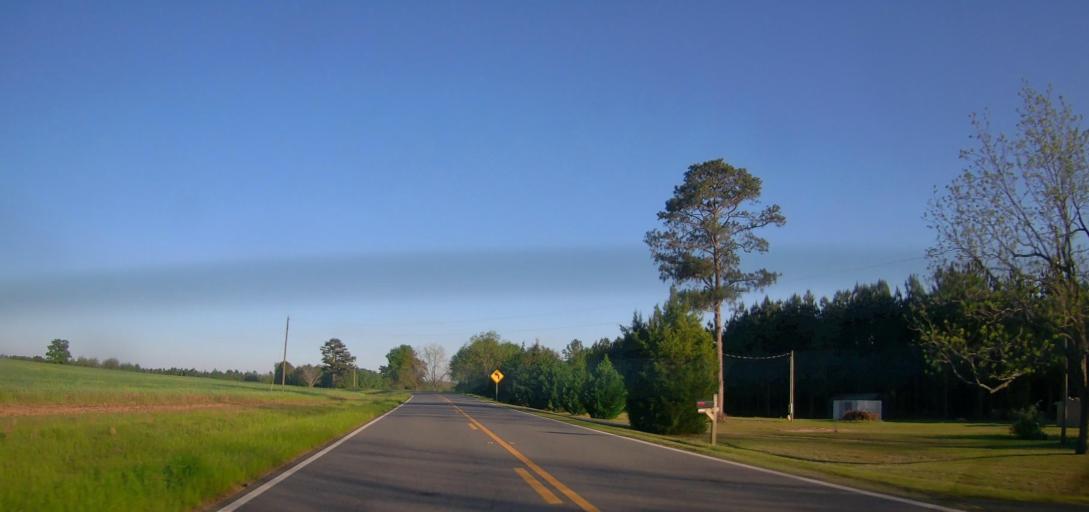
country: US
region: Georgia
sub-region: Marion County
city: Buena Vista
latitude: 32.3780
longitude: -84.4365
